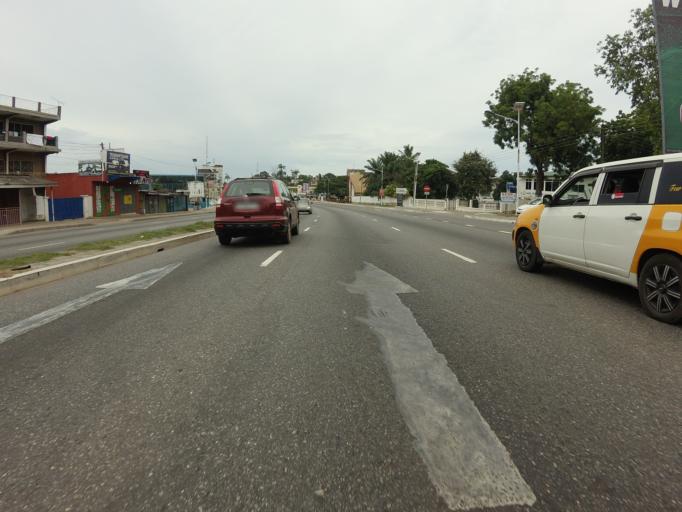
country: GH
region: Greater Accra
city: Dome
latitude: 5.6027
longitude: -0.2257
